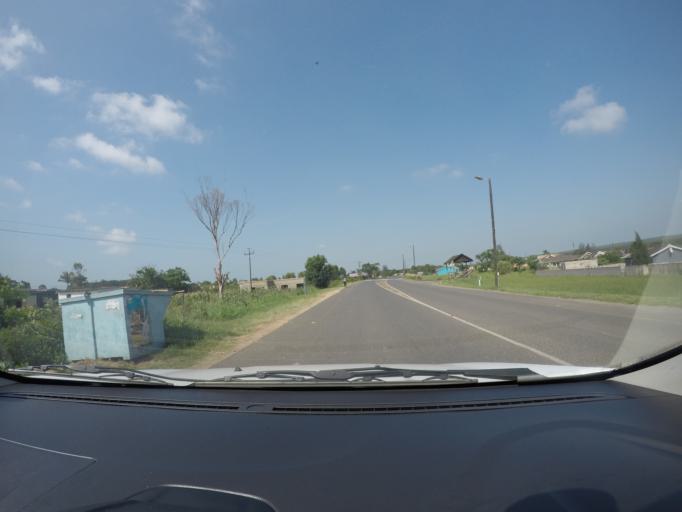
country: ZA
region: KwaZulu-Natal
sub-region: uThungulu District Municipality
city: eSikhawini
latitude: -28.8915
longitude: 31.8911
